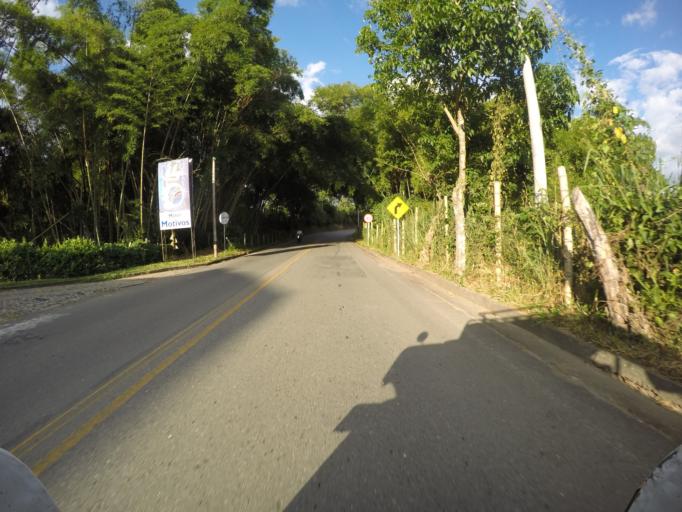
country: CO
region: Valle del Cauca
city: Alcala
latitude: 4.6831
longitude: -75.7992
